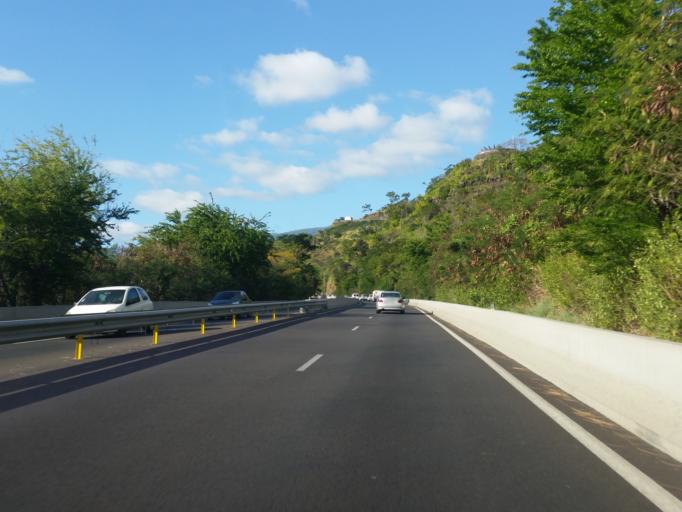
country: RE
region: Reunion
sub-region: Reunion
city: Saint-Denis
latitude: -20.8827
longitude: 55.4390
